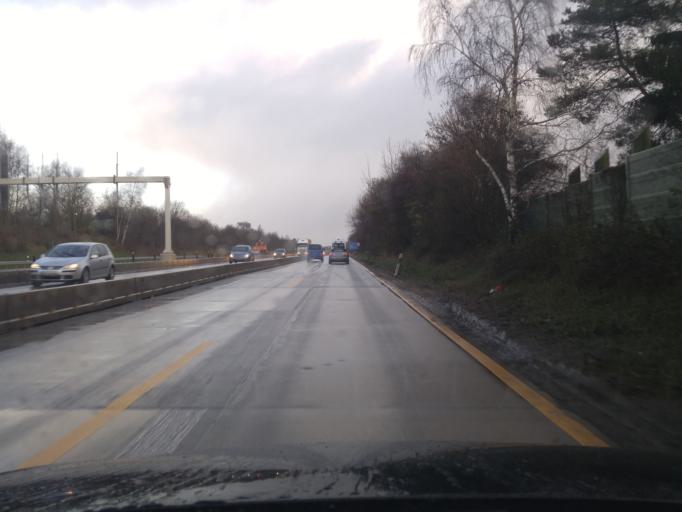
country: DE
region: Schleswig-Holstein
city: Stockelsdorf
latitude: 53.8861
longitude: 10.6669
